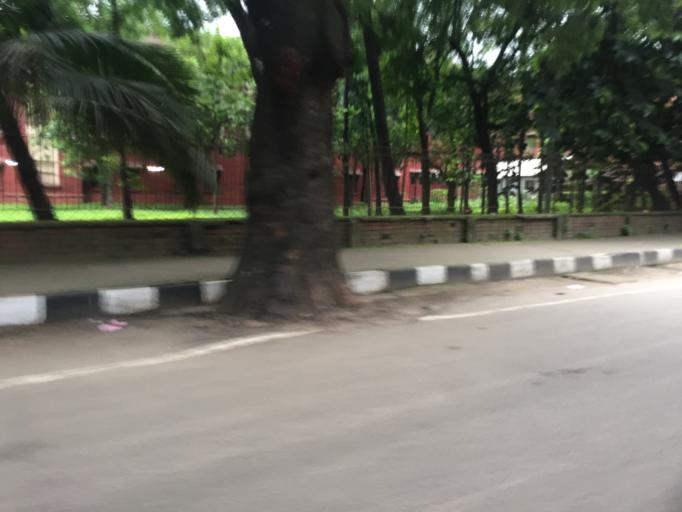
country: BD
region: Dhaka
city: Paltan
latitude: 23.7263
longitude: 90.4044
